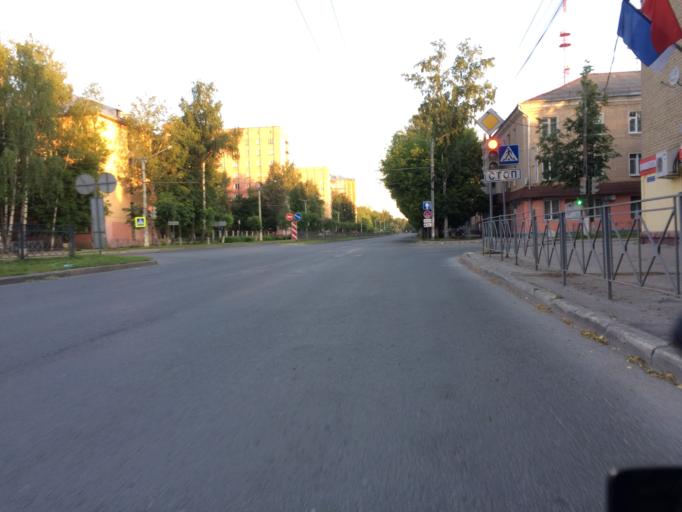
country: RU
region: Mariy-El
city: Yoshkar-Ola
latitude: 56.6427
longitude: 47.8860
